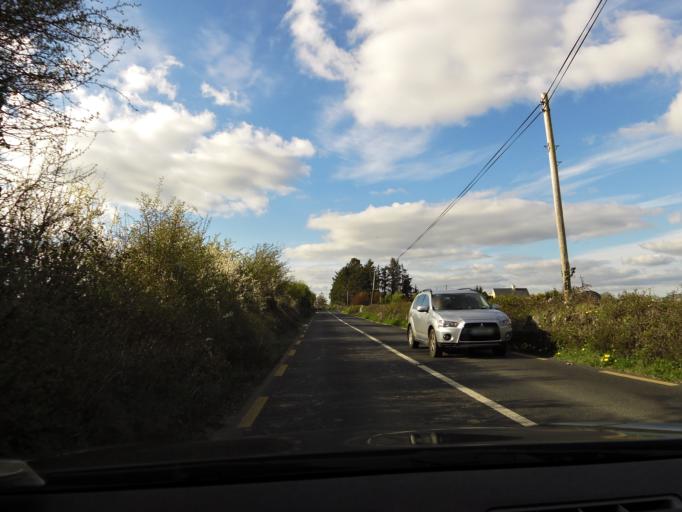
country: IE
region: Connaught
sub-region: County Galway
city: Portumna
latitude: 53.1190
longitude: -8.2399
